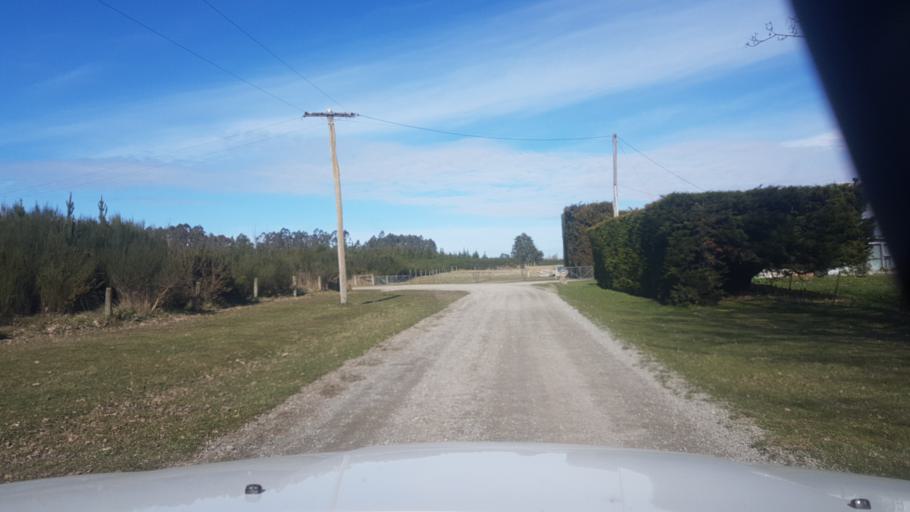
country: NZ
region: Canterbury
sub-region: Timaru District
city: Pleasant Point
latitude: -44.1361
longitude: 171.2736
